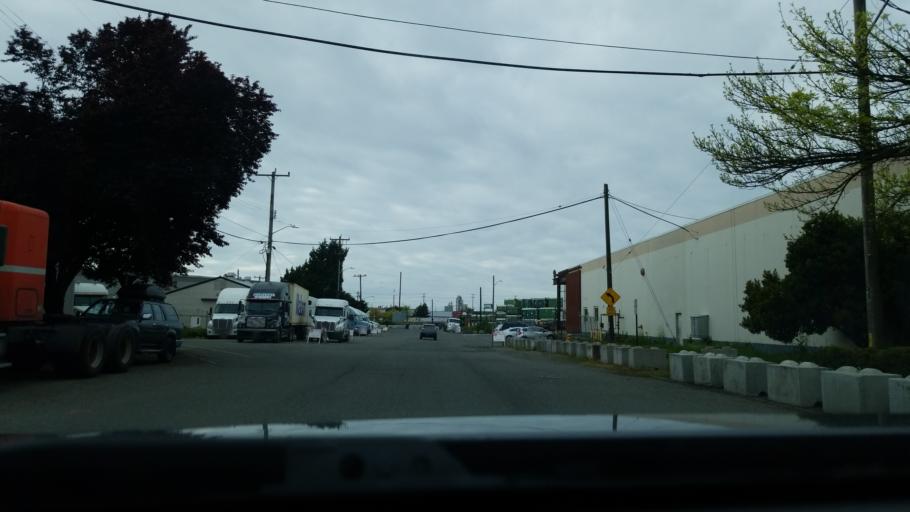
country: US
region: Washington
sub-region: King County
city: White Center
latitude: 47.5547
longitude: -122.3256
